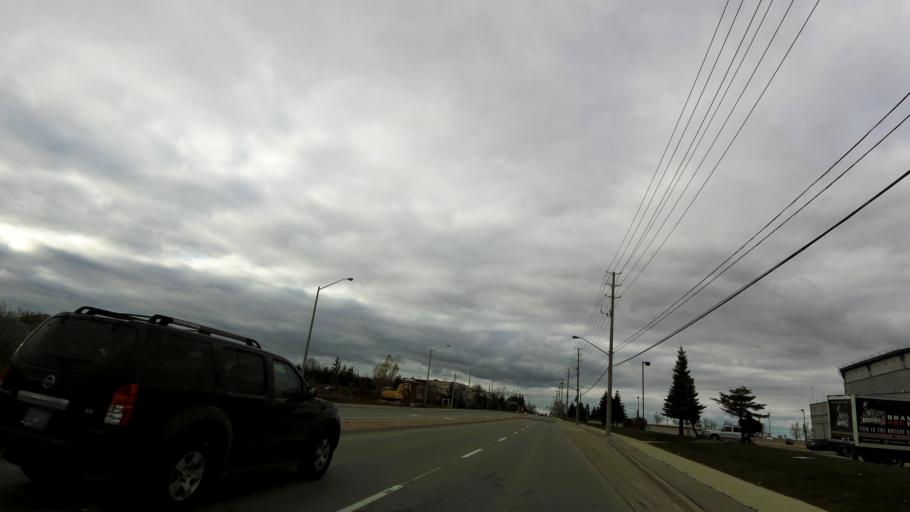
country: CA
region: Ontario
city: Brampton
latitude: 43.6661
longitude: -79.7088
